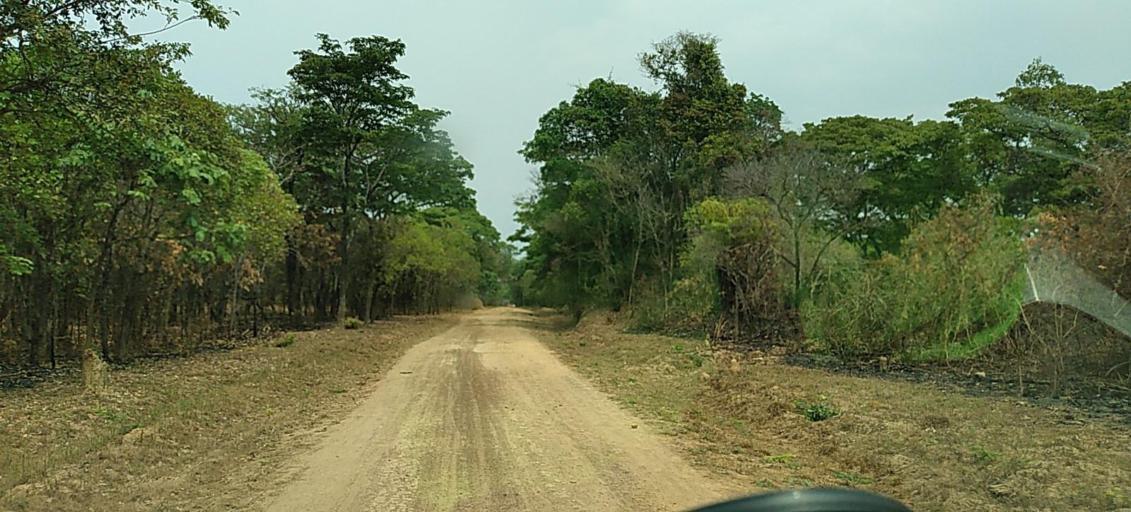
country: ZM
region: North-Western
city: Solwezi
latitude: -12.9519
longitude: 26.5622
